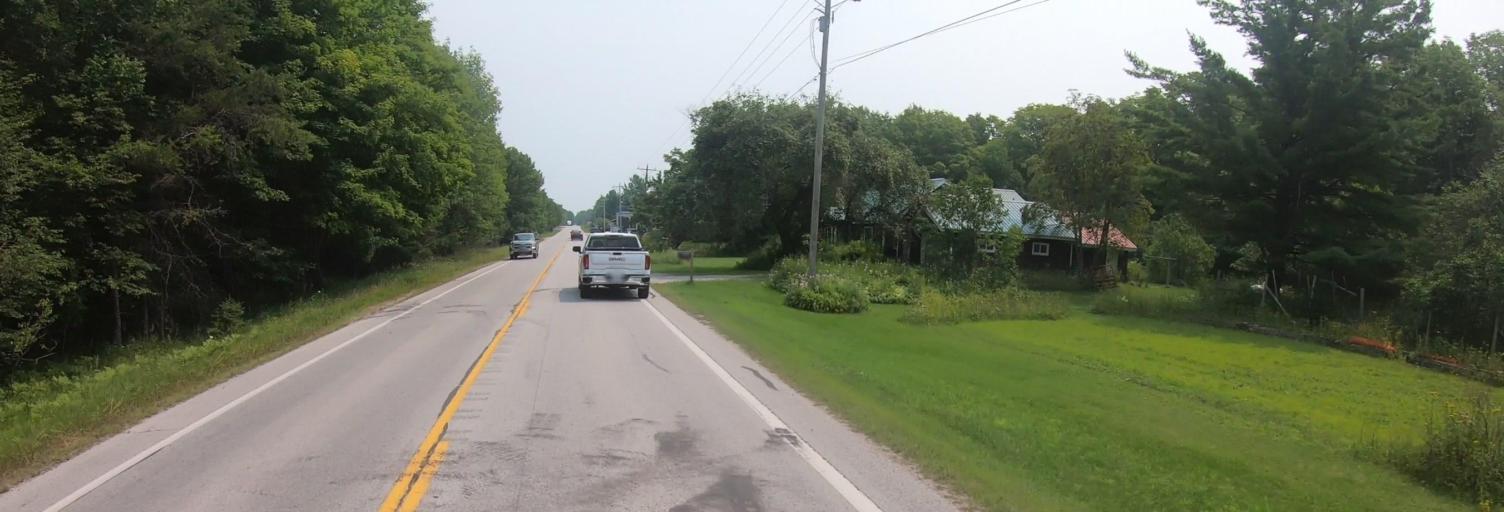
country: CA
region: Ontario
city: Thessalon
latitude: 45.9989
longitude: -83.7488
